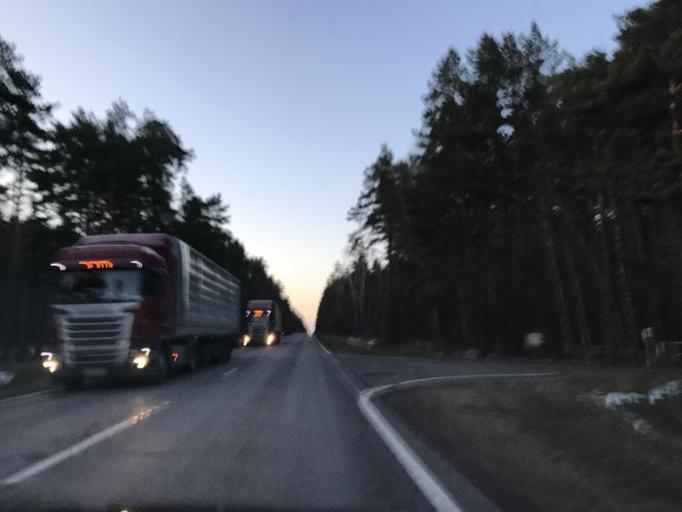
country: BY
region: Mogilev
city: Bykhaw
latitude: 53.4023
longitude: 30.3914
